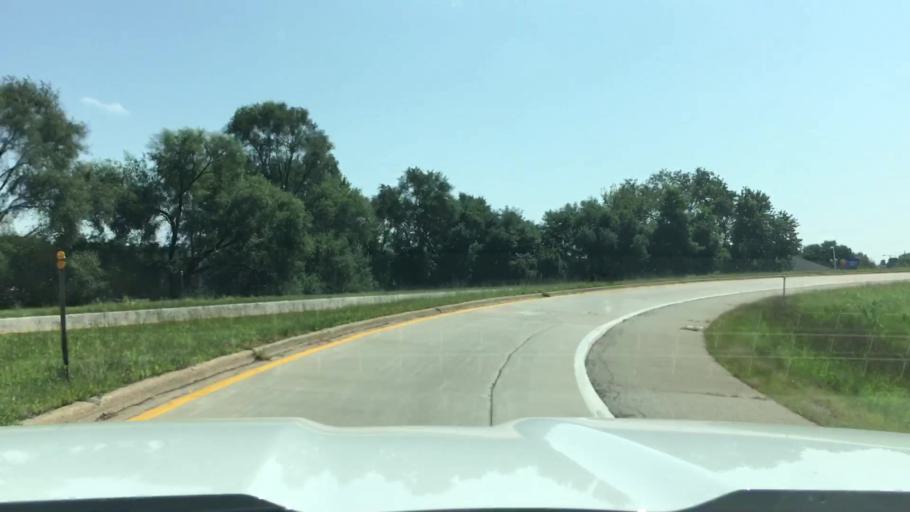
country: US
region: Michigan
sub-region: Allegan County
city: Plainwell
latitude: 42.4499
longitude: -85.6544
